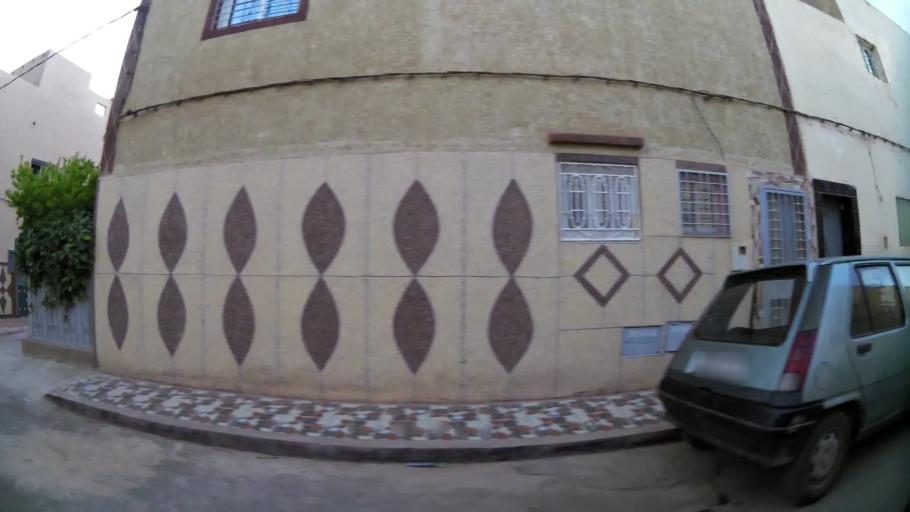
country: MA
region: Oriental
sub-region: Oujda-Angad
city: Oujda
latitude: 34.6819
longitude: -1.8831
